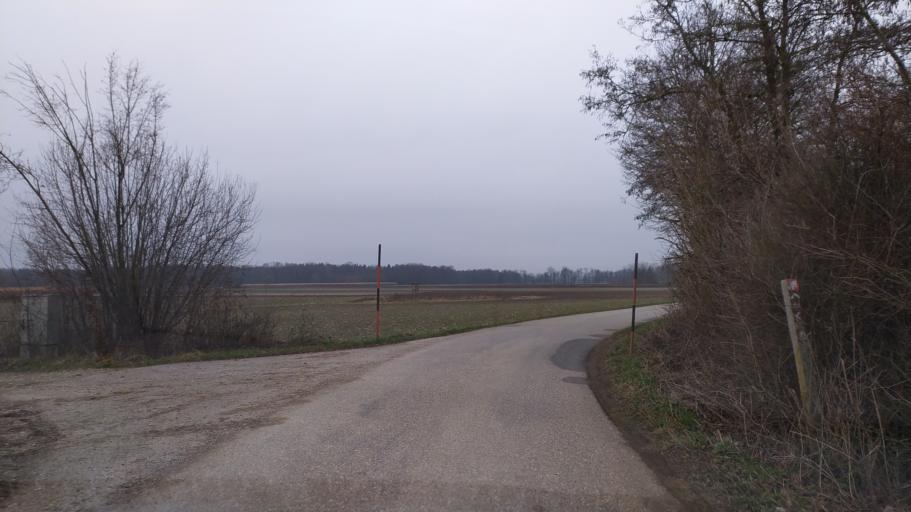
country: AT
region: Upper Austria
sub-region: Politischer Bezirk Perg
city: Perg
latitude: 48.2214
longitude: 14.7223
